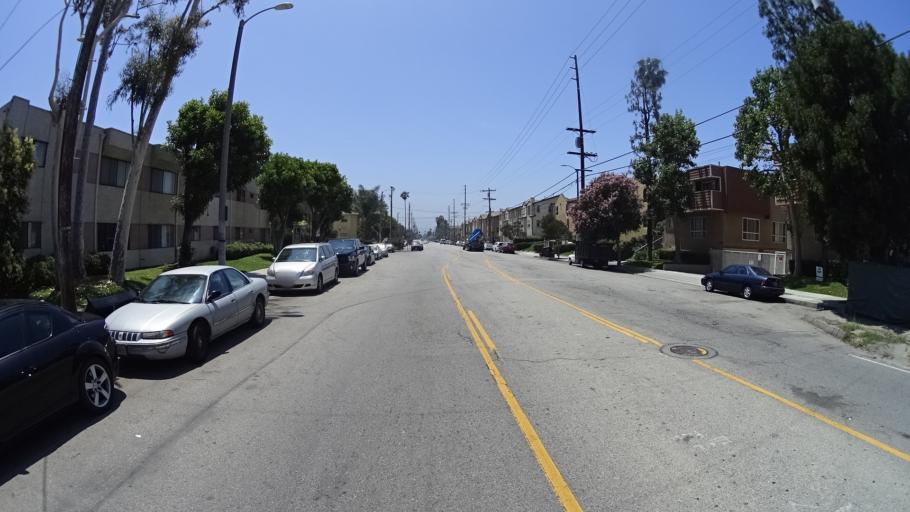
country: US
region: California
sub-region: Los Angeles County
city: Van Nuys
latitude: 34.2036
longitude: -118.4400
